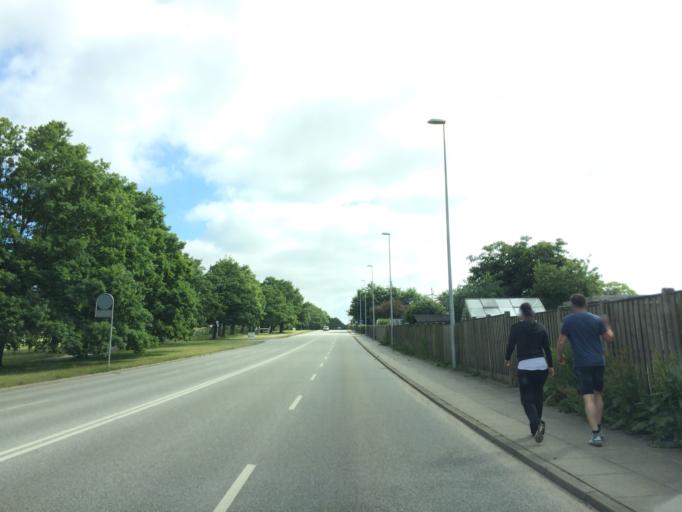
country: DK
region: Central Jutland
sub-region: Herning Kommune
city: Herning
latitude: 56.1427
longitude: 8.9430
